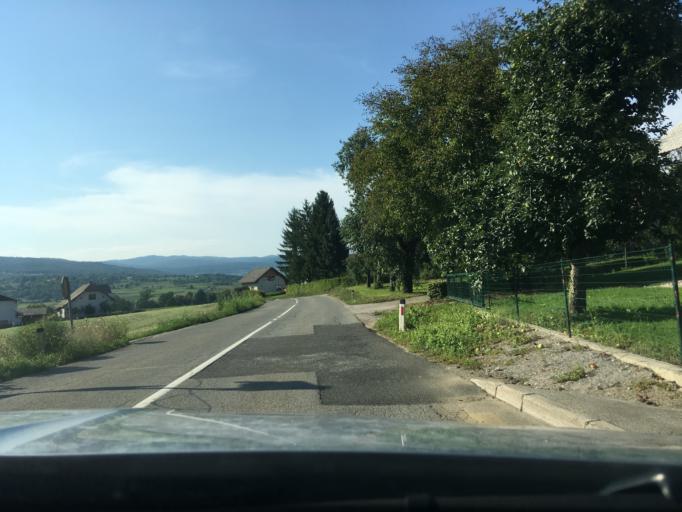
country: SI
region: Crnomelj
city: Crnomelj
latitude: 45.5198
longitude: 15.1751
